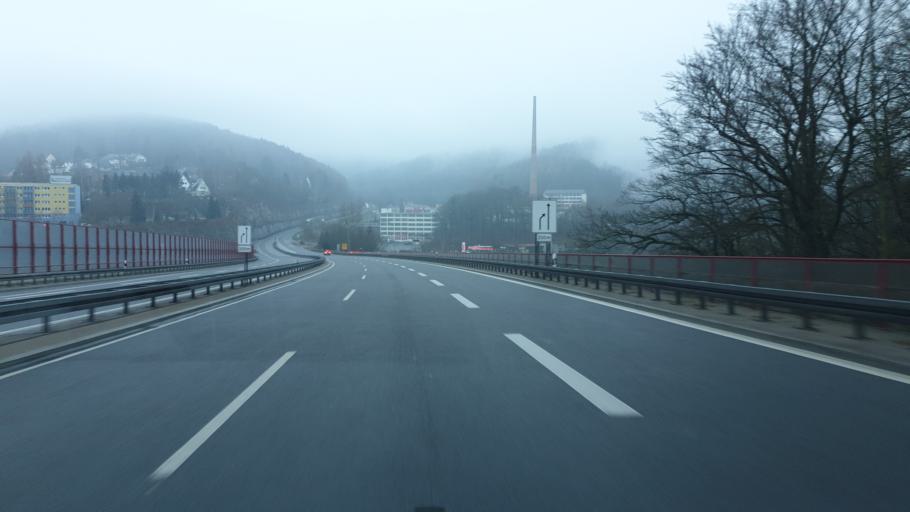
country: DE
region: Saxony
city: Zschopau
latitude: 50.7431
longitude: 13.0611
